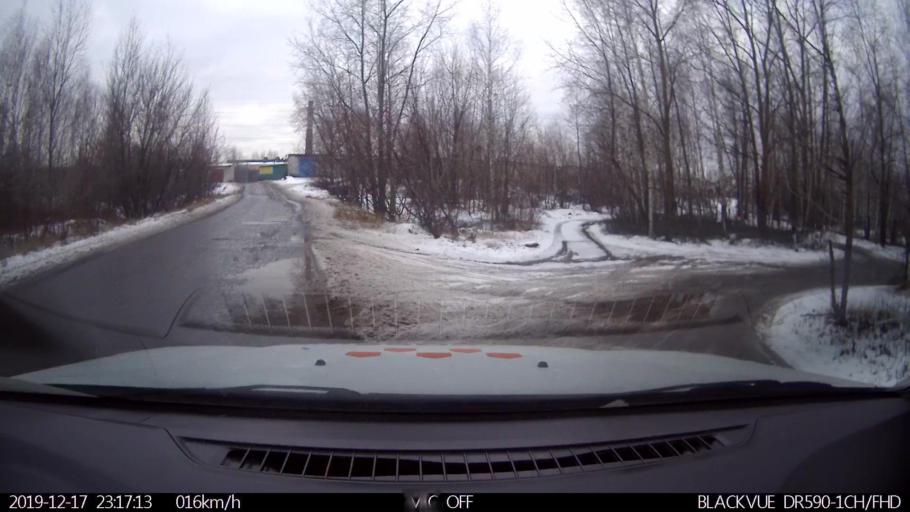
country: RU
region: Nizjnij Novgorod
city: Gorbatovka
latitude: 56.3536
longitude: 43.8250
